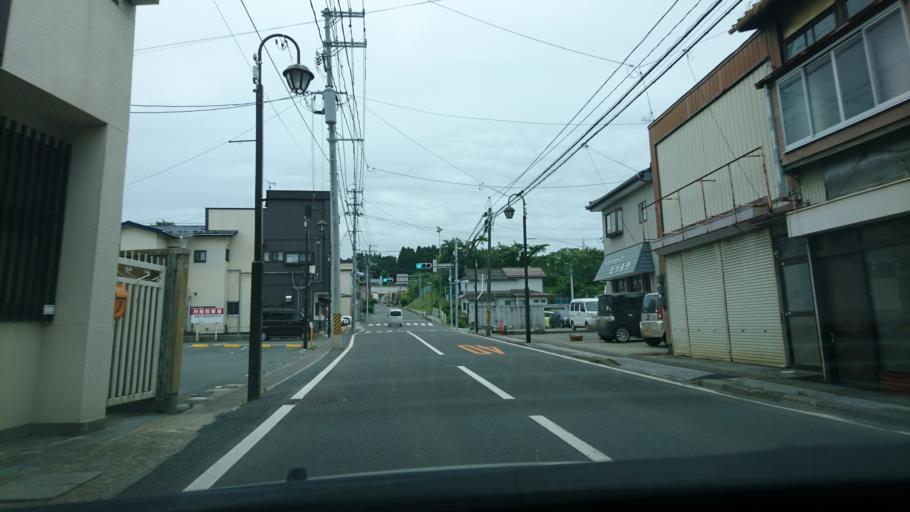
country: JP
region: Iwate
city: Ofunato
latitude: 38.7900
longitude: 141.5052
